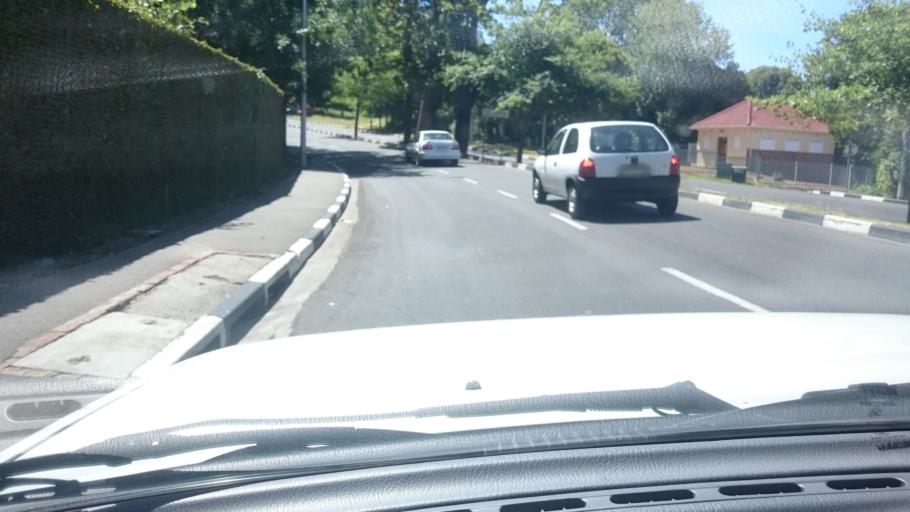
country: ZA
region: Western Cape
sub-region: City of Cape Town
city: Claremont
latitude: -34.0013
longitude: 18.4592
